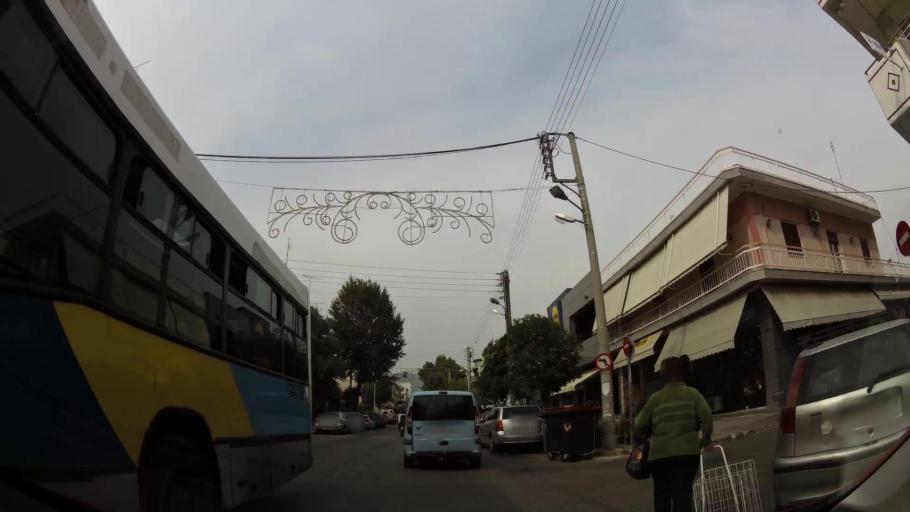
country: GR
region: Attica
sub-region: Nomarchia Athinas
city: Peristeri
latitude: 38.0097
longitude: 23.6801
